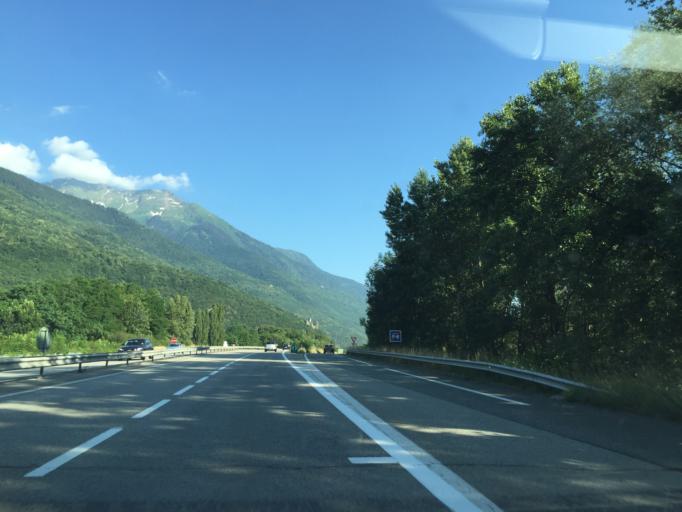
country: FR
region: Rhone-Alpes
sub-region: Departement de la Savoie
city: La Bathie
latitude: 45.6535
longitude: 6.4344
